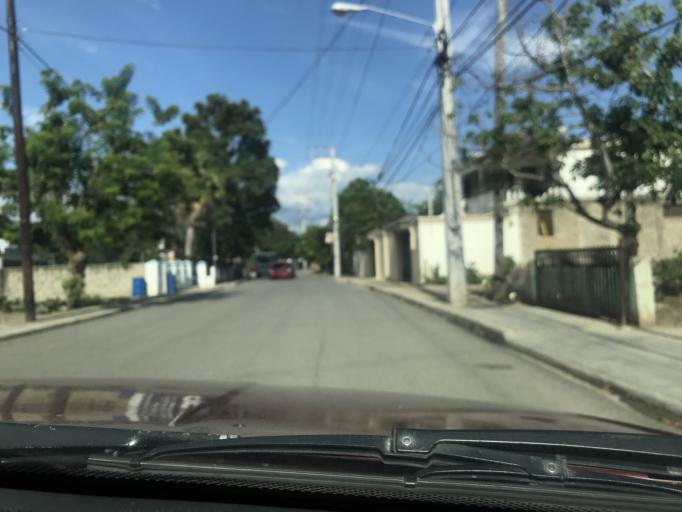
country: DO
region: Santiago
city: Licey al Medio
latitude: 19.4057
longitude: -70.6287
